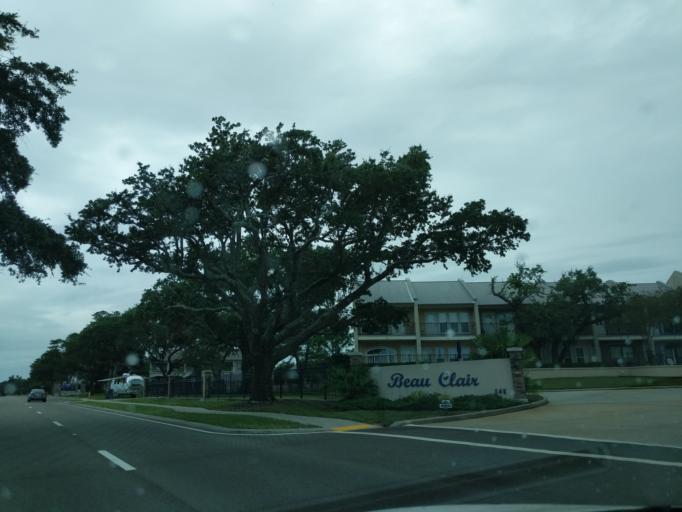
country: US
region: Mississippi
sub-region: Harrison County
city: Long Beach
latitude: 30.3404
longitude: -89.1637
